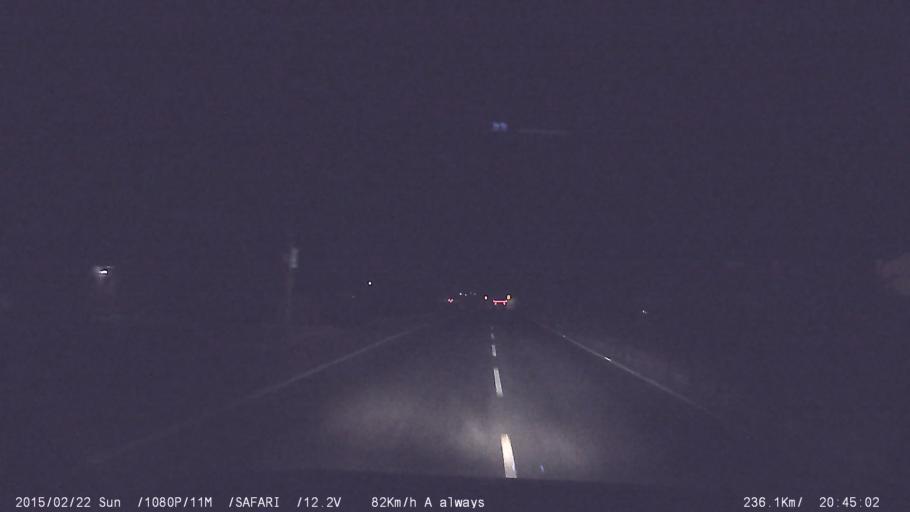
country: IN
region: Tamil Nadu
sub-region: Dindigul
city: Vedasandur
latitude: 10.4638
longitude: 77.9471
